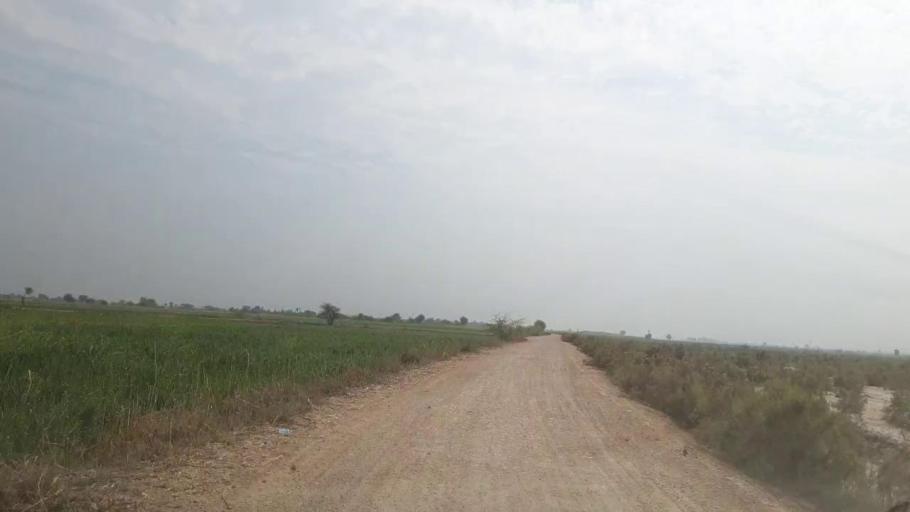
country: PK
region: Sindh
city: Mirpur Khas
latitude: 25.5458
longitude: 69.1257
